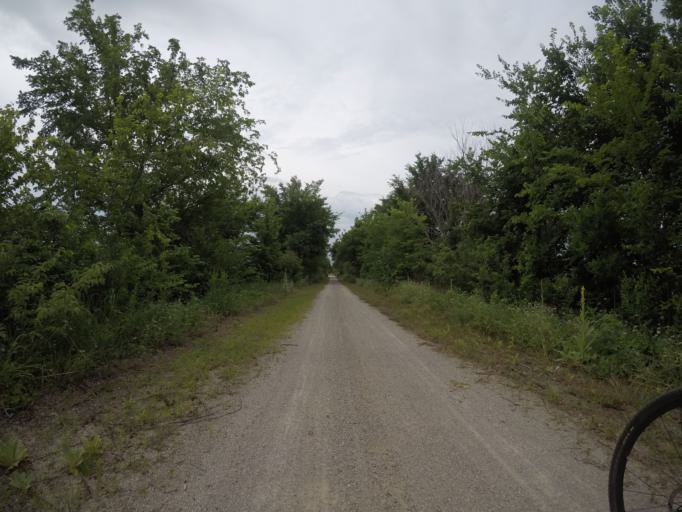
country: US
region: Kansas
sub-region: Franklin County
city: Ottawa
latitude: 38.5224
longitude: -95.2723
